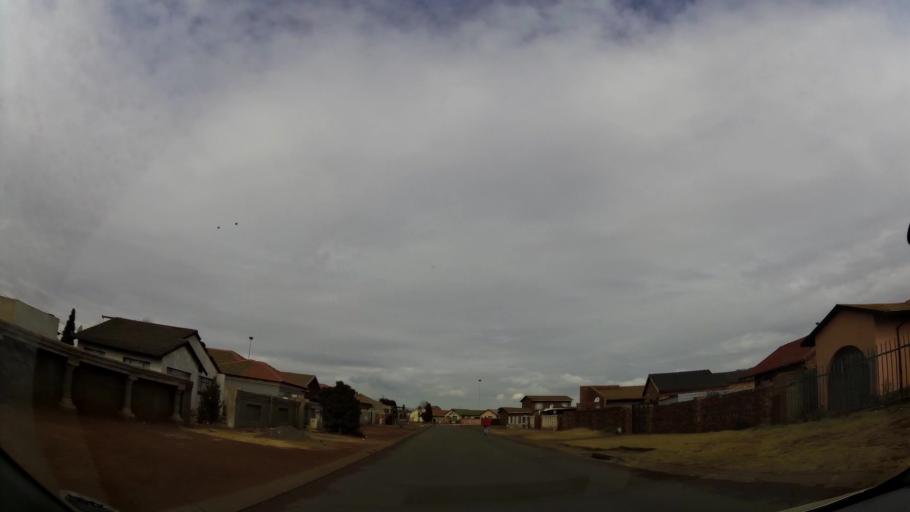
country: ZA
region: Gauteng
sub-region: Ekurhuleni Metropolitan Municipality
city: Germiston
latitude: -26.3752
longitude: 28.1551
